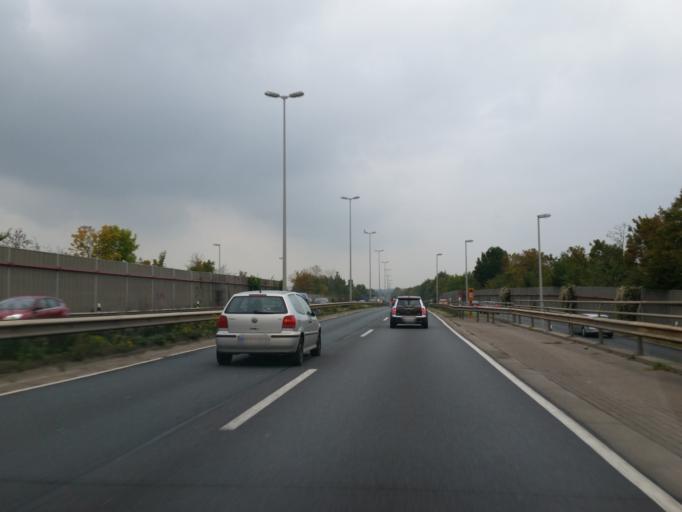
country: DE
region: Lower Saxony
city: Braunschweig
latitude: 52.2543
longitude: 10.4940
